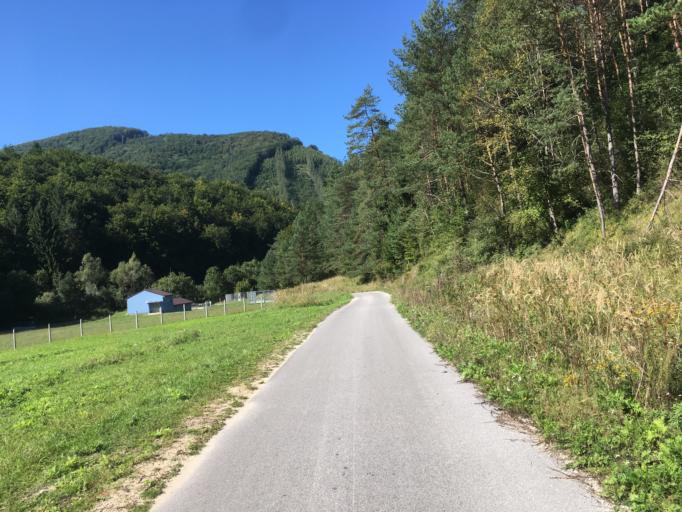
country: SK
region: Trenciansky
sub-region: Okres Povazska Bystrica
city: Povazska Bystrica
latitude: 49.0132
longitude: 18.4434
